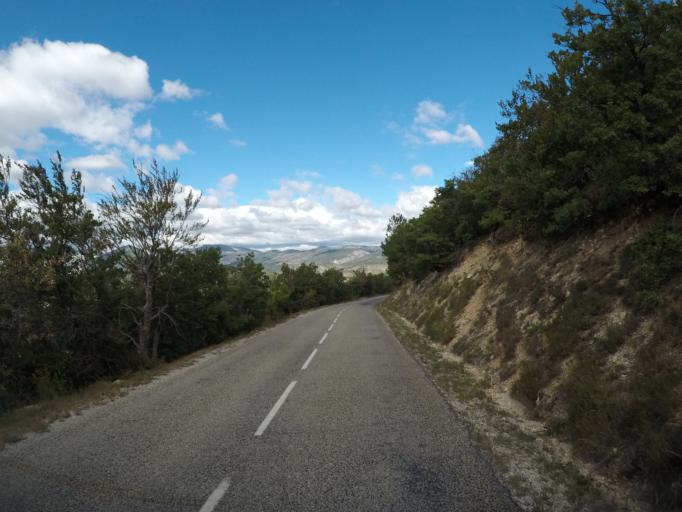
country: FR
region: Provence-Alpes-Cote d'Azur
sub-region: Departement du Vaucluse
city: Sault
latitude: 44.1577
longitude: 5.4412
